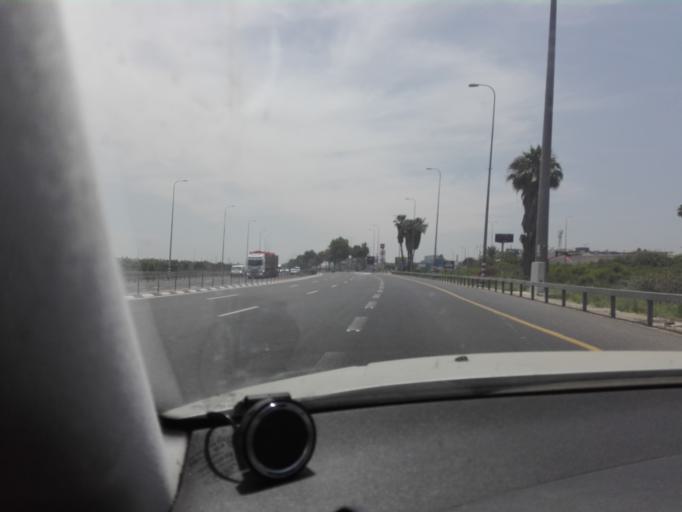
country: IL
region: Central District
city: Bene 'Ayish
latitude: 31.7324
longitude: 34.7575
